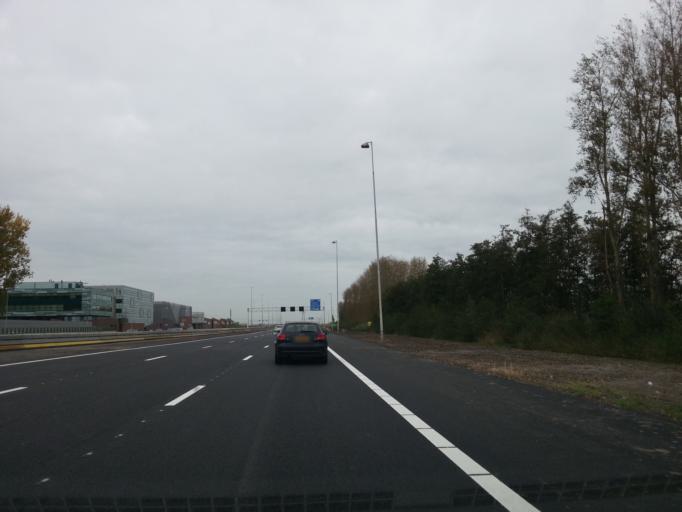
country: NL
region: South Holland
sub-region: Gemeente Leiderdorp
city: Leiderdorp
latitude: 52.1537
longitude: 4.5402
